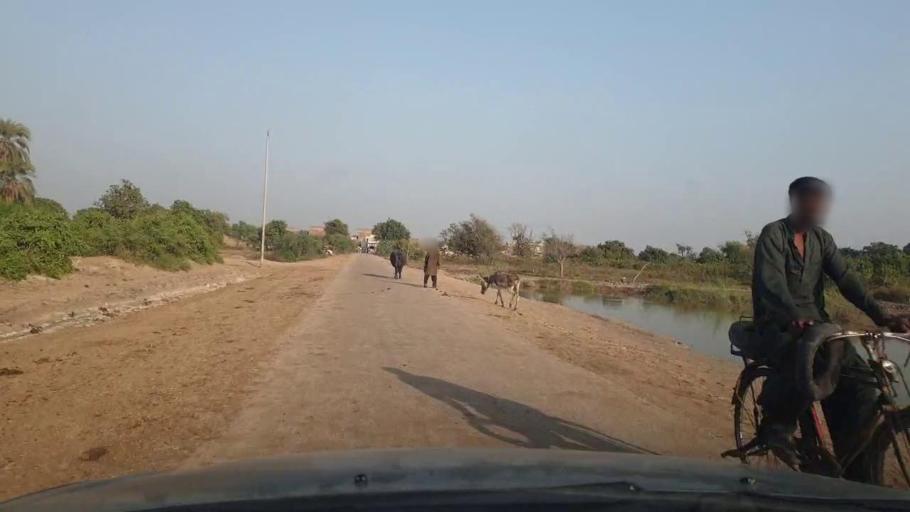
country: PK
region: Sindh
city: Hyderabad
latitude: 25.4513
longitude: 68.4262
